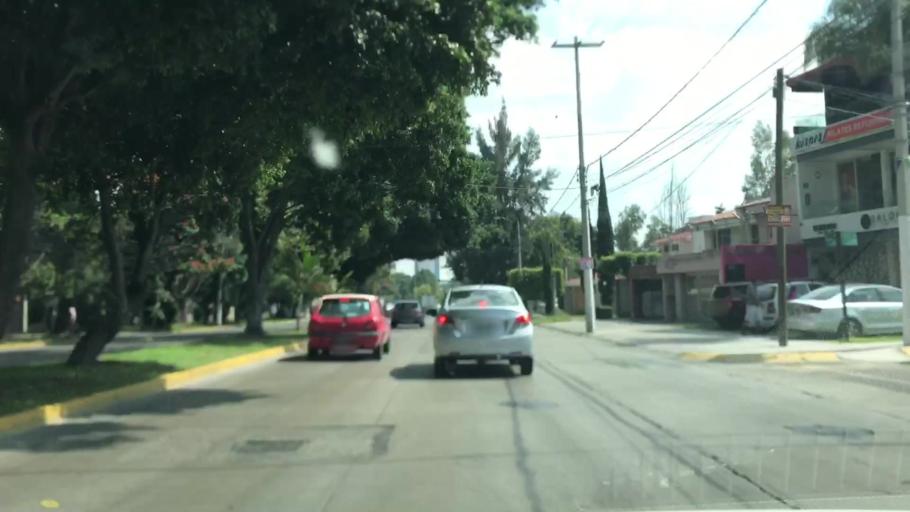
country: MX
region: Jalisco
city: Guadalajara
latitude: 20.6649
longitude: -103.4099
